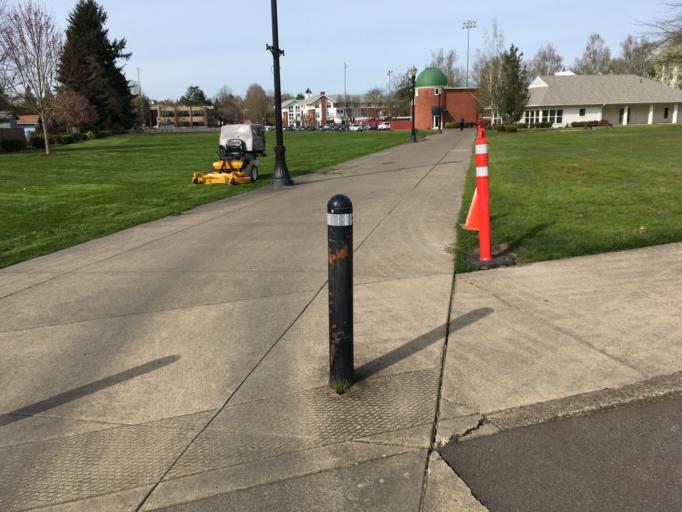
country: US
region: Oregon
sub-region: Yamhill County
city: McMinnville
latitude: 45.1970
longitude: -123.2007
